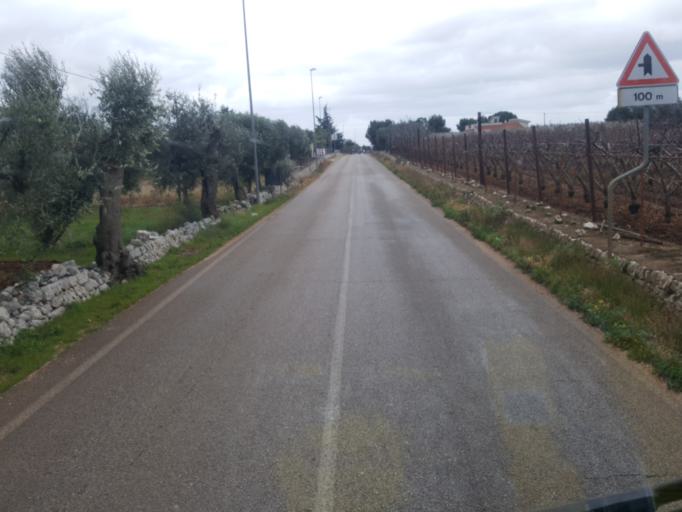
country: IT
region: Apulia
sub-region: Provincia di Bari
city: Conversano
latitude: 40.9569
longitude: 17.0996
